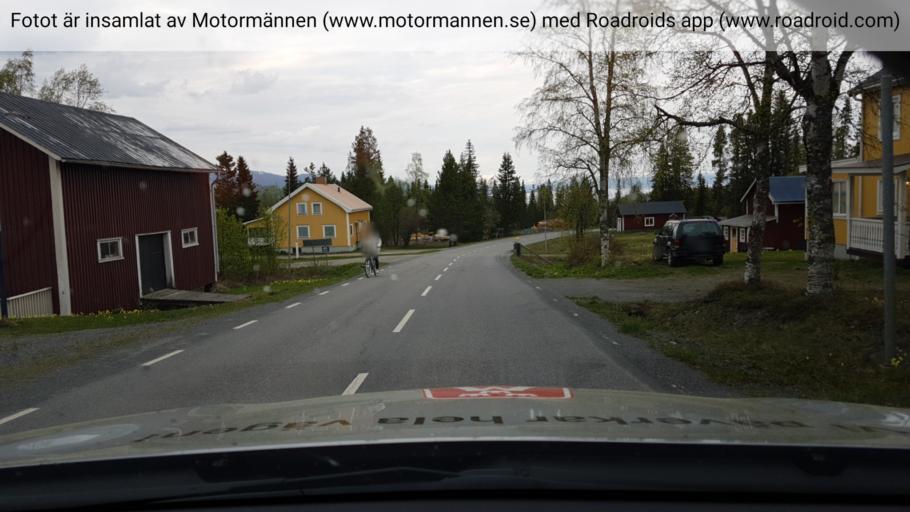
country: SE
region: Jaemtland
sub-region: Are Kommun
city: Are
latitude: 63.5596
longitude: 13.0272
